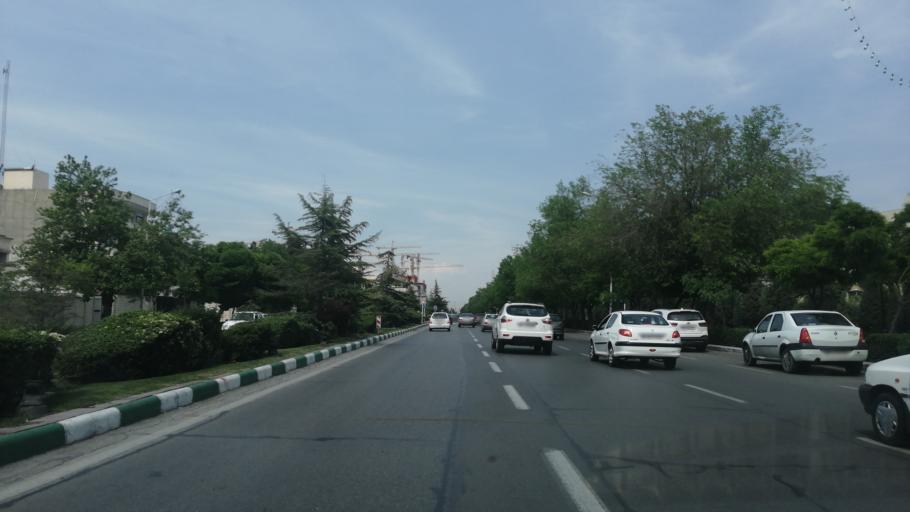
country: IR
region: Razavi Khorasan
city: Mashhad
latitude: 36.3114
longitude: 59.5565
